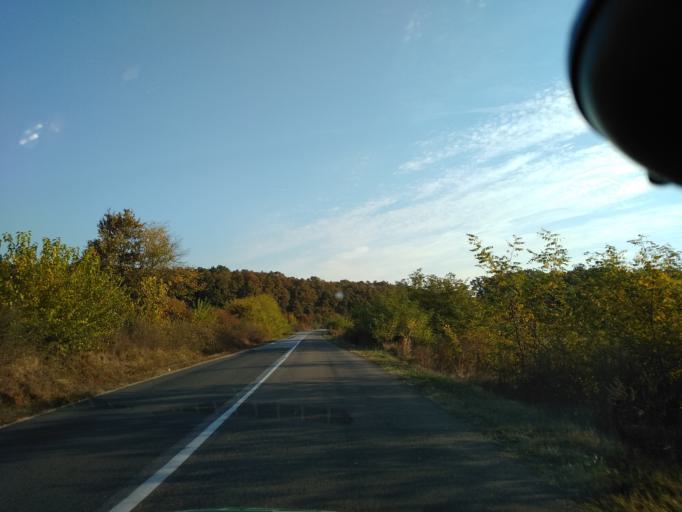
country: RO
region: Timis
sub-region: Comuna Pischia
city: Pischia
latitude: 45.9168
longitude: 21.3544
